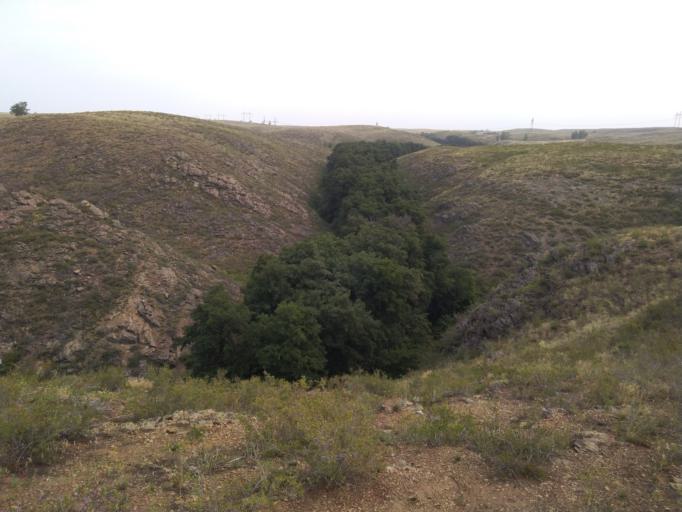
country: RU
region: Orenburg
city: Staraya Akkermanovka
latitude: 51.2399
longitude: 58.1341
